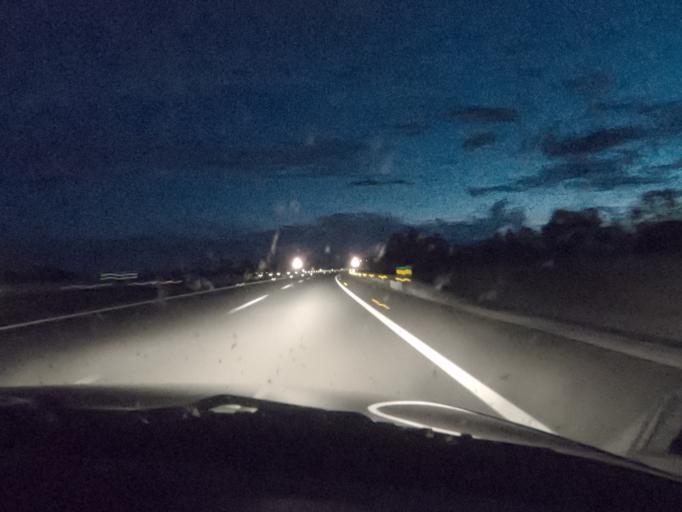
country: ES
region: Extremadura
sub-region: Provincia de Caceres
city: Galisteo
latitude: 39.9769
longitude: -6.3291
